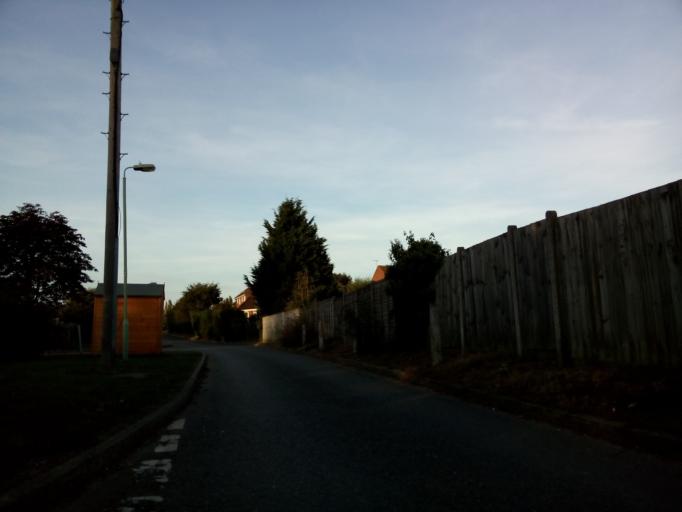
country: GB
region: England
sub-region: Suffolk
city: Bramford
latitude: 52.0402
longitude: 1.1069
